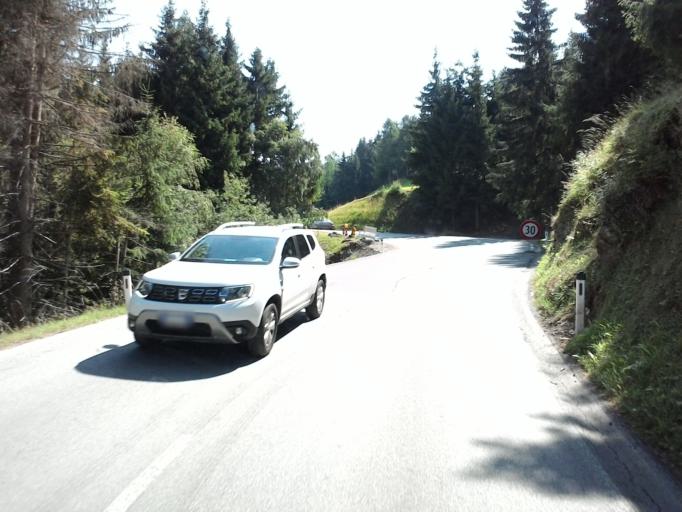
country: AT
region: Tyrol
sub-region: Politischer Bezirk Lienz
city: Strassen
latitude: 46.7410
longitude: 12.4690
